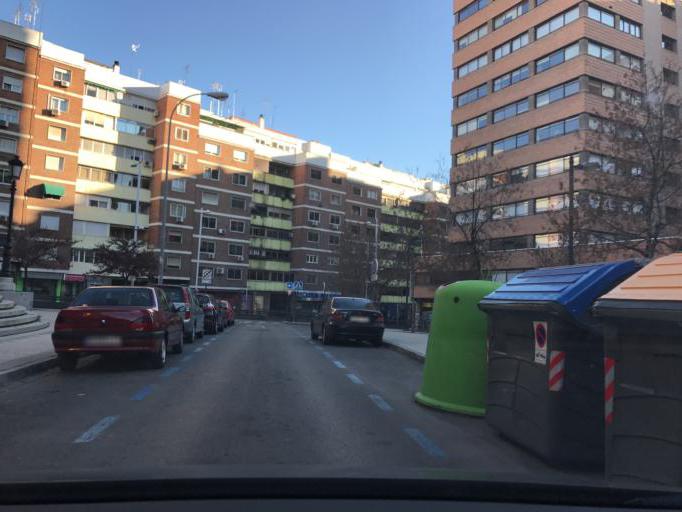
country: ES
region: Andalusia
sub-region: Provincia de Granada
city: Granada
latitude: 37.1862
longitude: -3.6046
